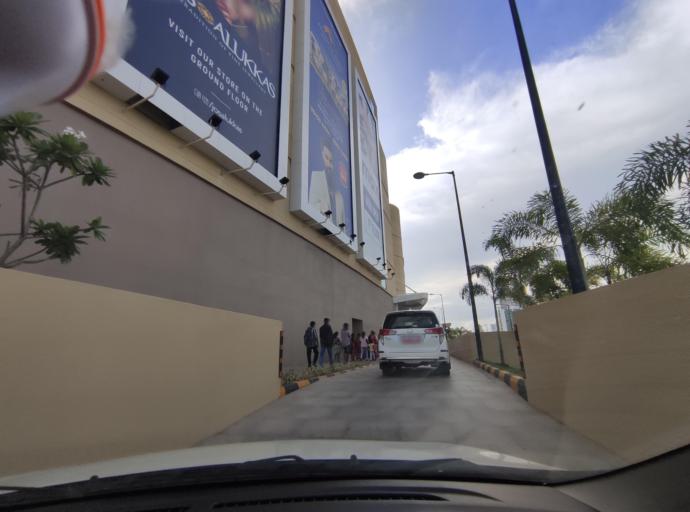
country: IN
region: Kerala
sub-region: Thiruvananthapuram
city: Thiruvananthapuram
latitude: 8.5148
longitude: 76.8991
